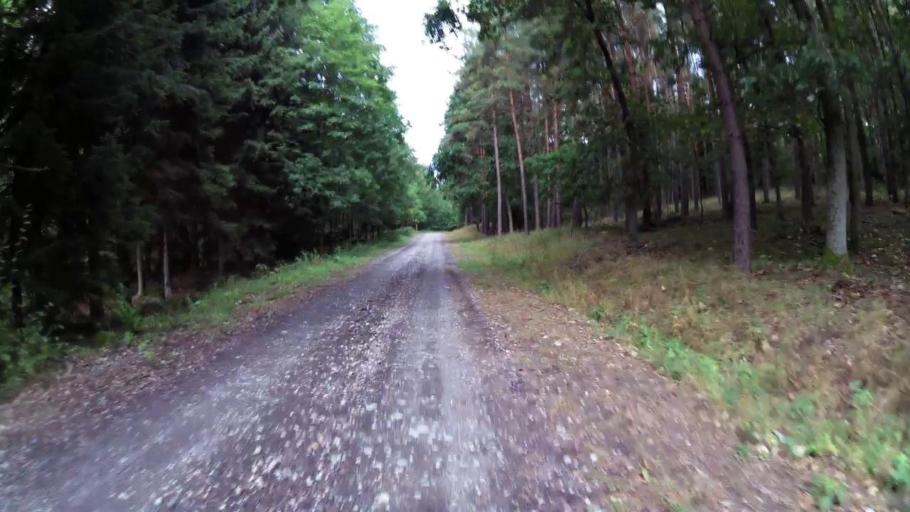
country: PL
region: West Pomeranian Voivodeship
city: Trzcinsko Zdroj
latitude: 52.8853
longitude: 14.6801
